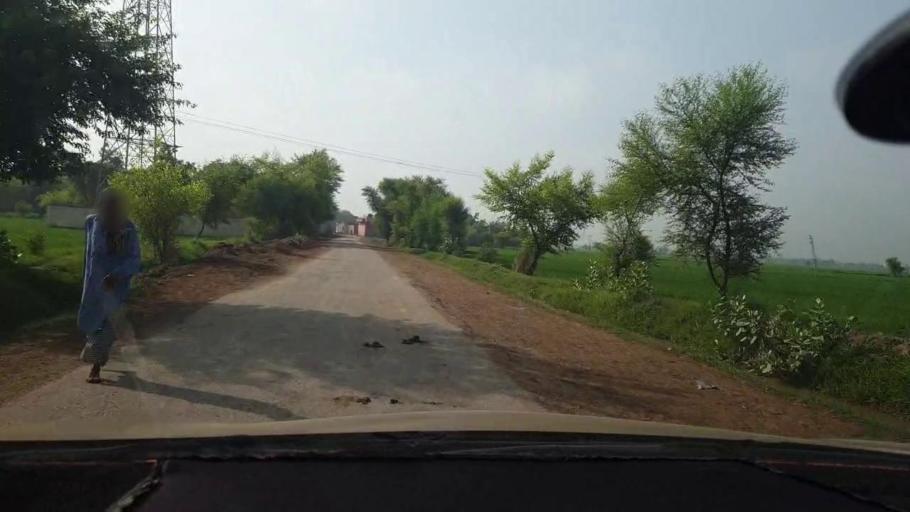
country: PK
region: Sindh
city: Goth Garelo
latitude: 27.4897
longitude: 68.0105
